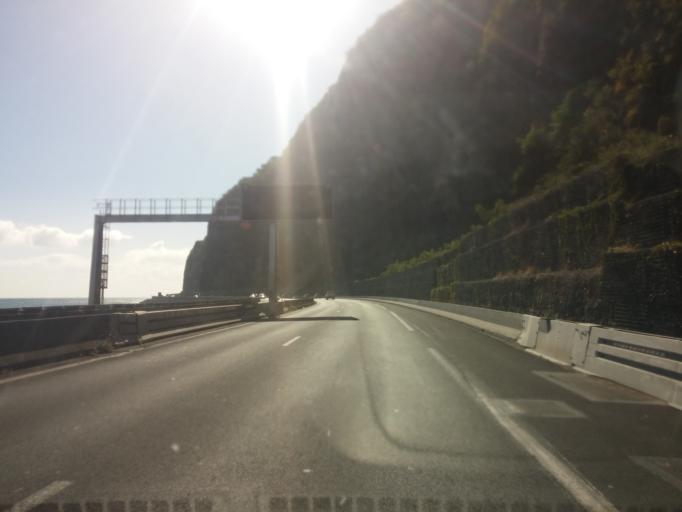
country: RE
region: Reunion
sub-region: Reunion
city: La Possession
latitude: -20.9196
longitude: 55.3477
